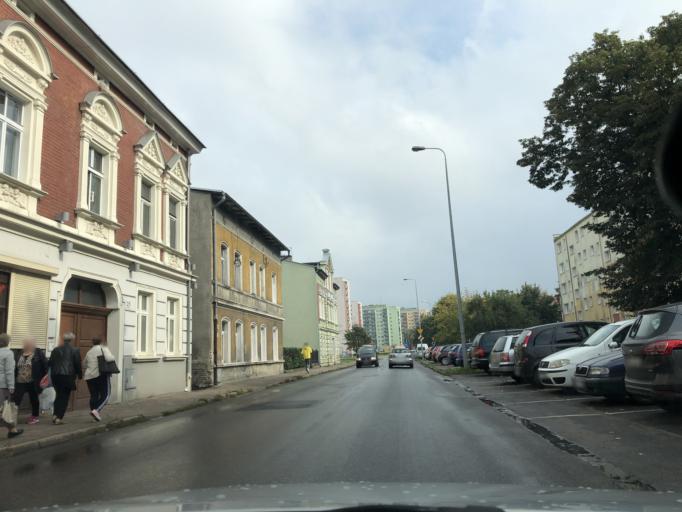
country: PL
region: Greater Poland Voivodeship
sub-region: Powiat pilski
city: Pila
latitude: 53.1509
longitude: 16.7532
